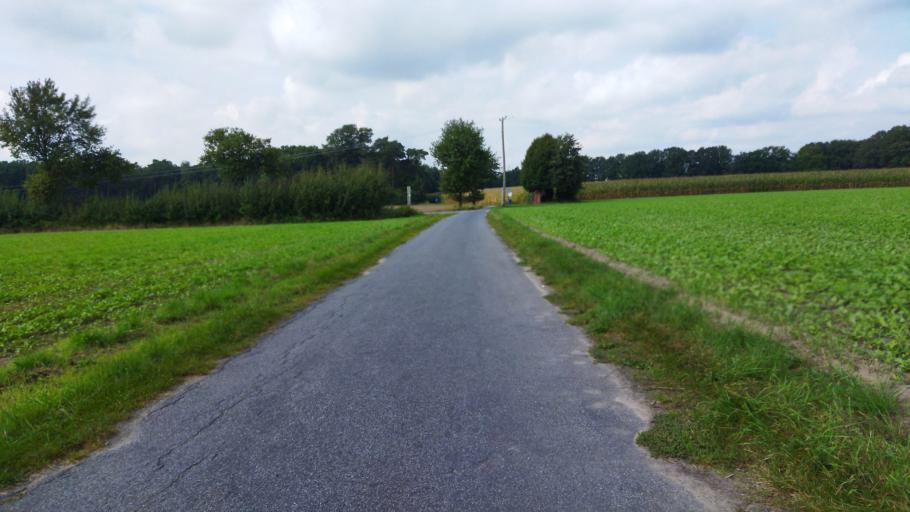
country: DE
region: North Rhine-Westphalia
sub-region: Regierungsbezirk Munster
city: Everswinkel
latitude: 51.9637
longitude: 7.9094
